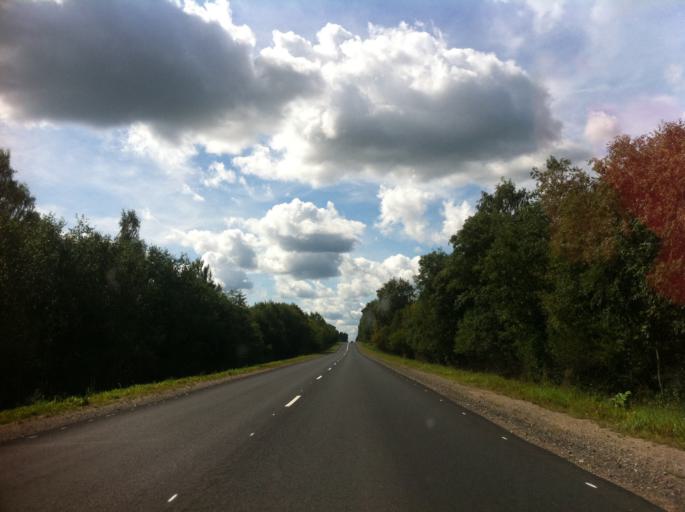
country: RU
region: Pskov
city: Izborsk
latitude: 57.7225
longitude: 27.9418
